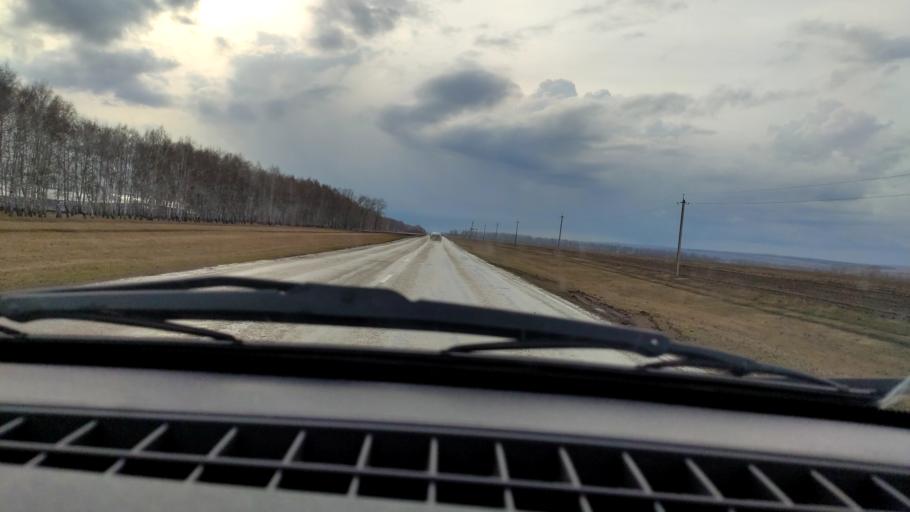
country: RU
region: Bashkortostan
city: Kushnarenkovo
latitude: 55.1045
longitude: 55.0213
